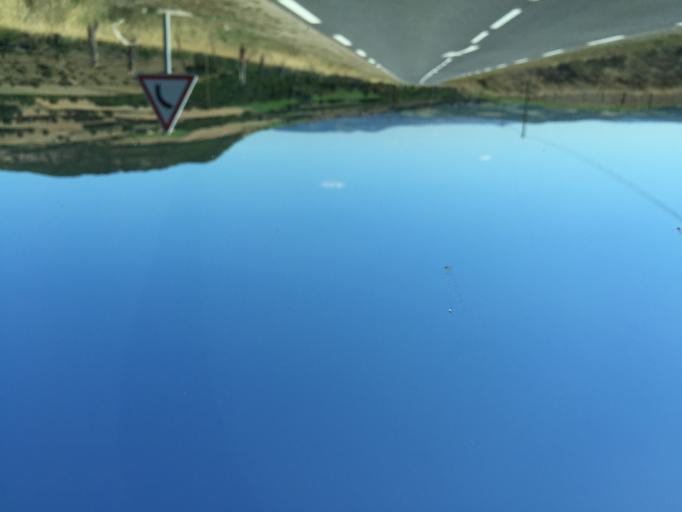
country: FR
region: Midi-Pyrenees
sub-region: Departement de l'Aveyron
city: Saint-Georges-de-Luzencon
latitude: 44.0120
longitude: 3.0002
